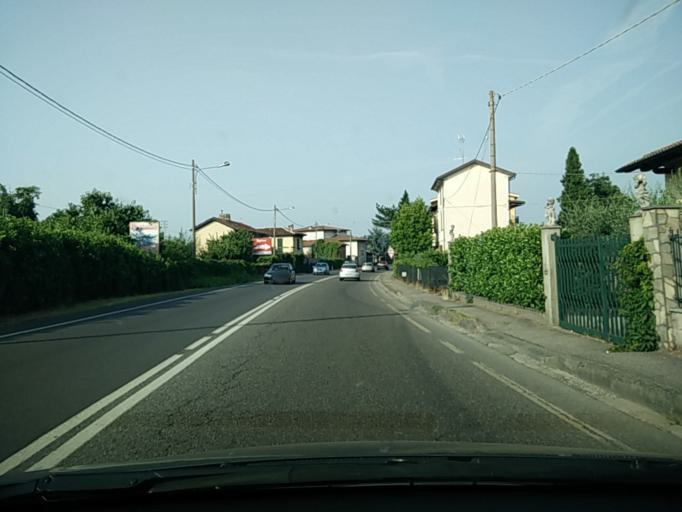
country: IT
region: Lombardy
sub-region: Provincia di Pavia
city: Broni
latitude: 45.0737
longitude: 9.2716
